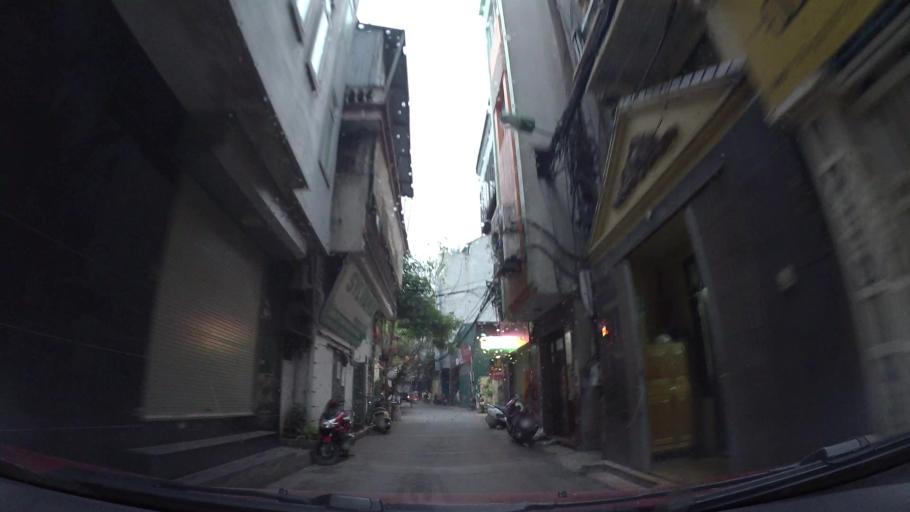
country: VN
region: Ha Noi
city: Hanoi
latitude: 21.0231
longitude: 105.8393
